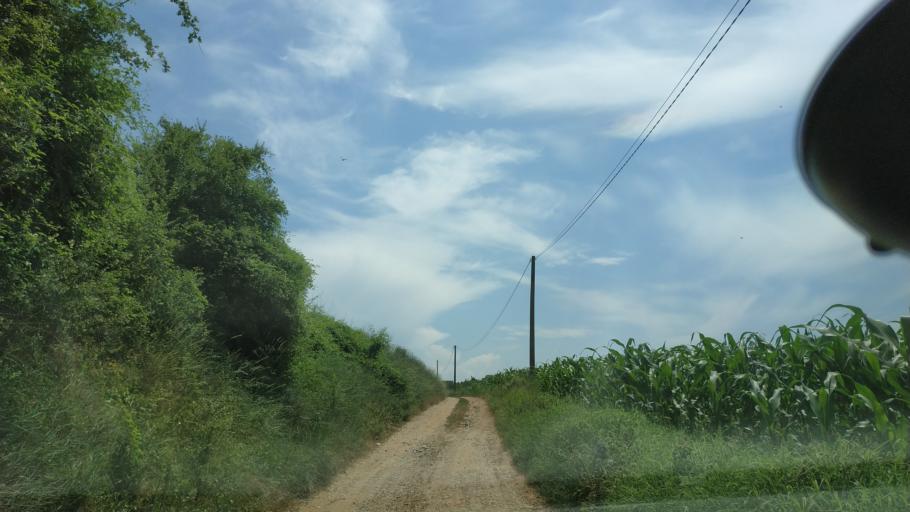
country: RS
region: Central Serbia
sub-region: Nisavski Okrug
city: Aleksinac
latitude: 43.5724
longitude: 21.7045
